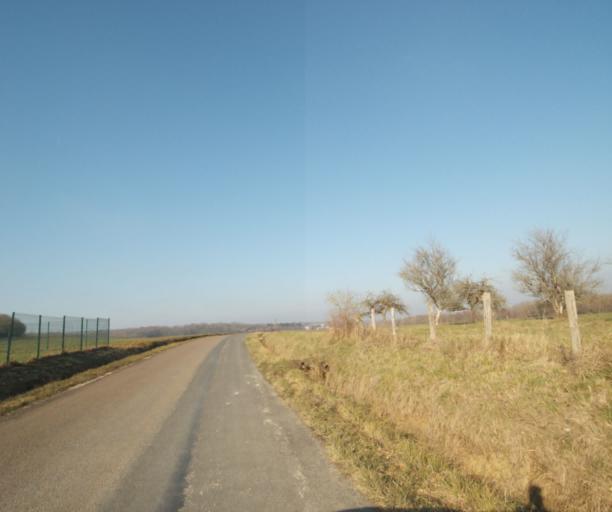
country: FR
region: Champagne-Ardenne
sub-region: Departement de la Haute-Marne
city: Wassy
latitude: 48.5010
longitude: 4.9292
